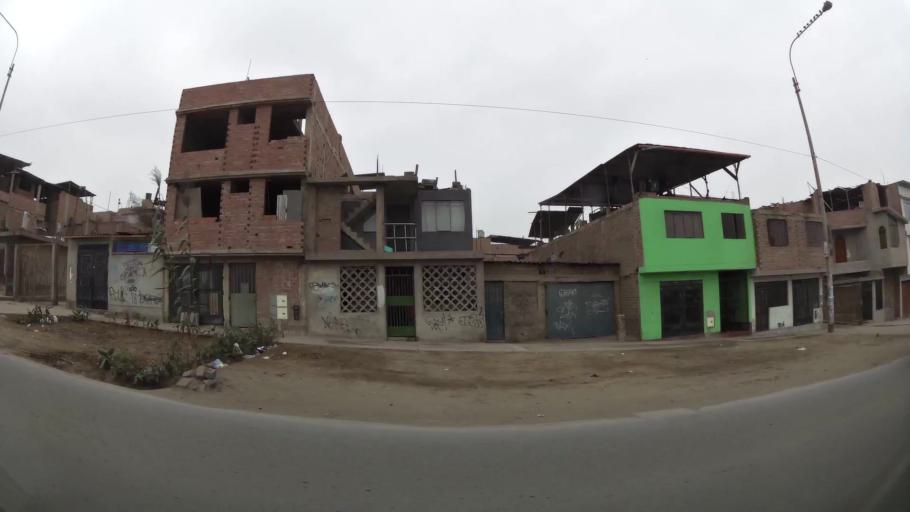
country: PE
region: Lima
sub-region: Lima
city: Surco
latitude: -12.2283
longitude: -76.9206
